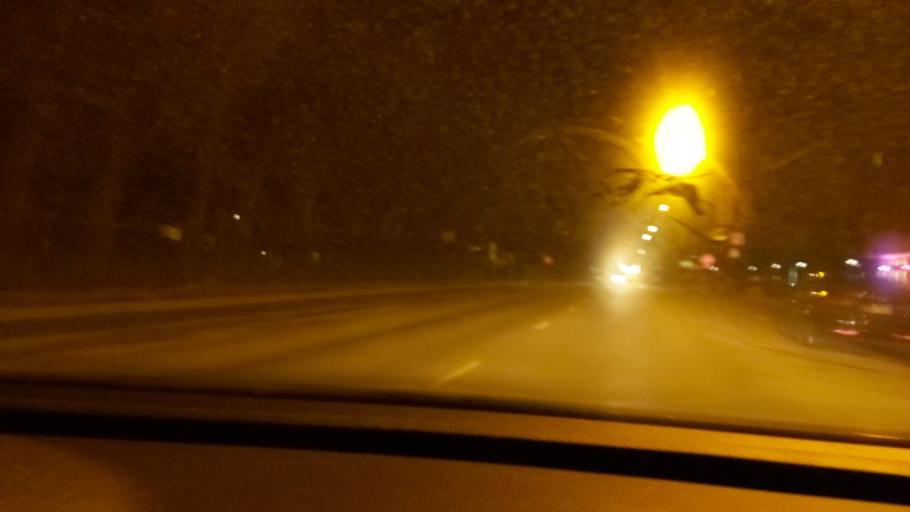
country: US
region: Illinois
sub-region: Cook County
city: Lincolnwood
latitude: 41.9829
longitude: -87.7194
